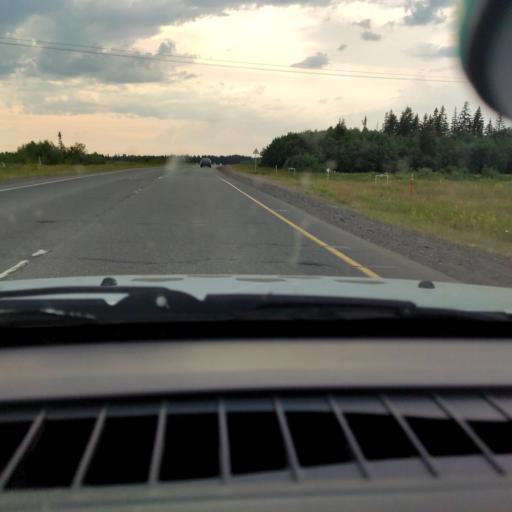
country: RU
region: Udmurtiya
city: Debesy
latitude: 57.6048
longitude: 53.4508
